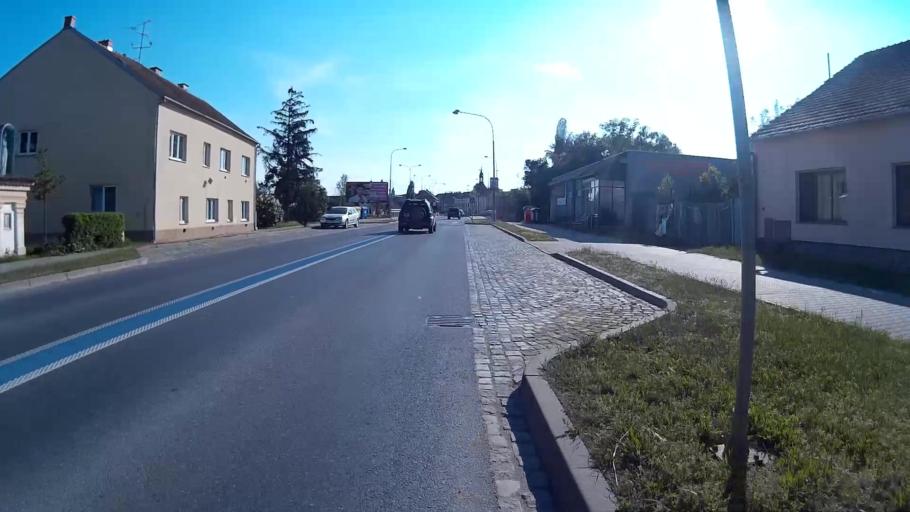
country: CZ
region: South Moravian
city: Pohorelice
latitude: 48.9837
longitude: 16.5277
